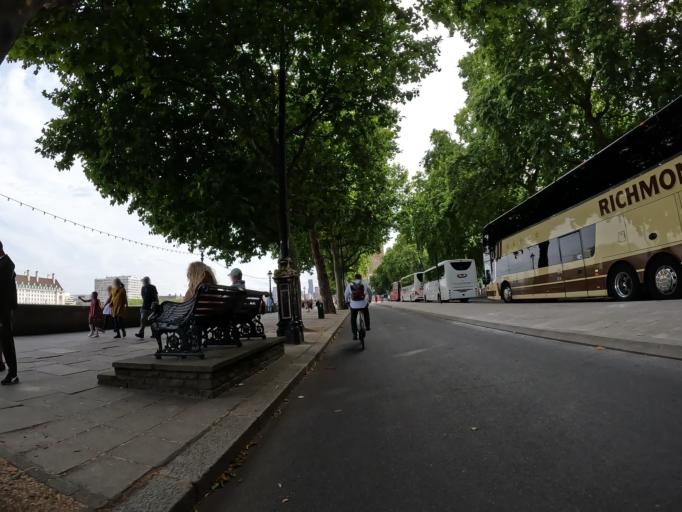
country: GB
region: England
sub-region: Greater London
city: Bromley
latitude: 51.4212
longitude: 0.0189
